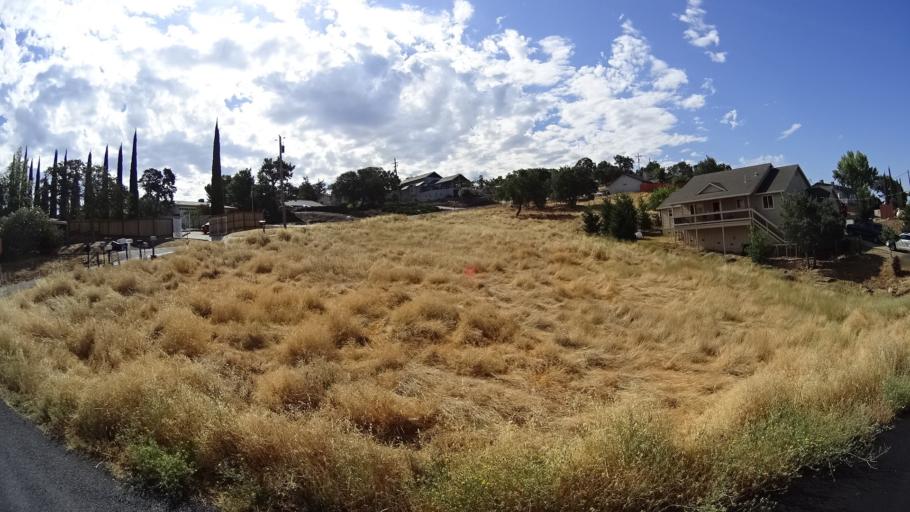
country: US
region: California
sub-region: Calaveras County
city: Copperopolis
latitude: 37.9146
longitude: -120.6165
